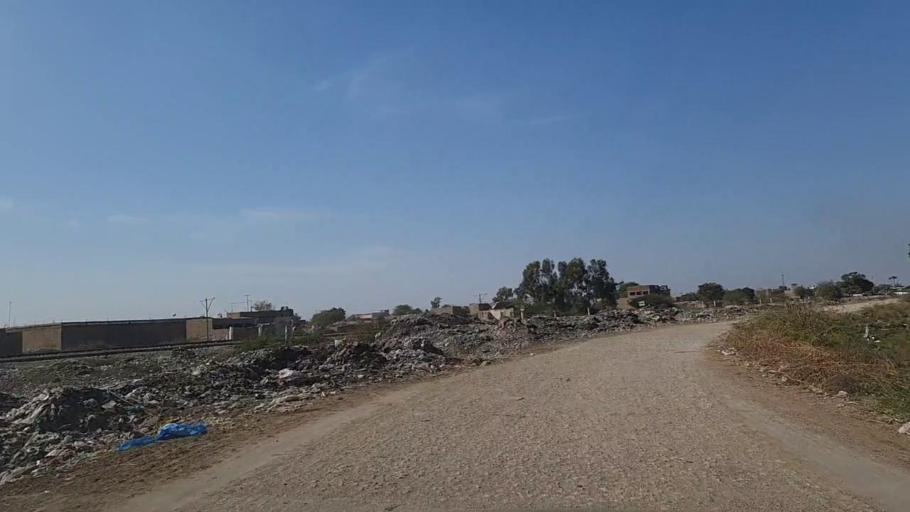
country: PK
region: Sindh
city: Nawabshah
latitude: 26.2242
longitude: 68.4216
